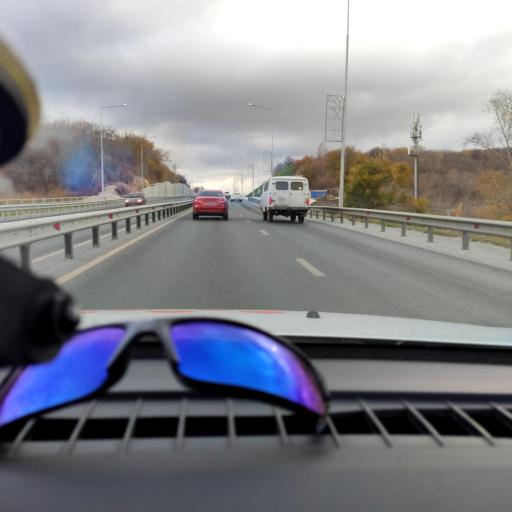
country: RU
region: Samara
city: Volzhskiy
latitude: 53.3713
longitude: 50.1828
